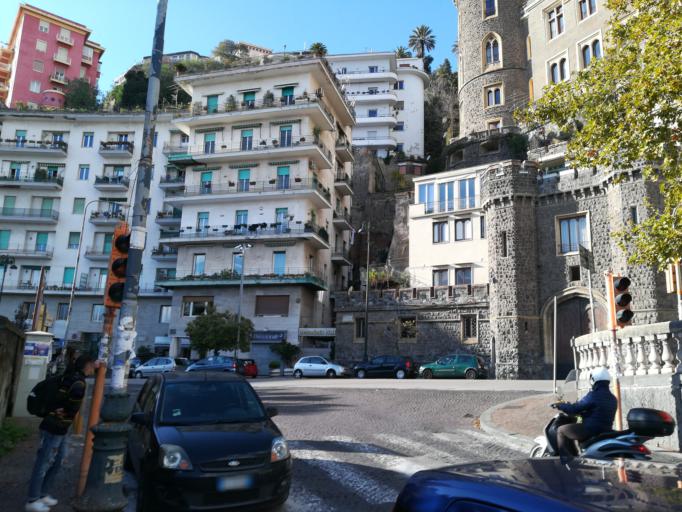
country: IT
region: Campania
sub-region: Provincia di Napoli
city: Napoli
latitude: 40.8385
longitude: 14.2332
